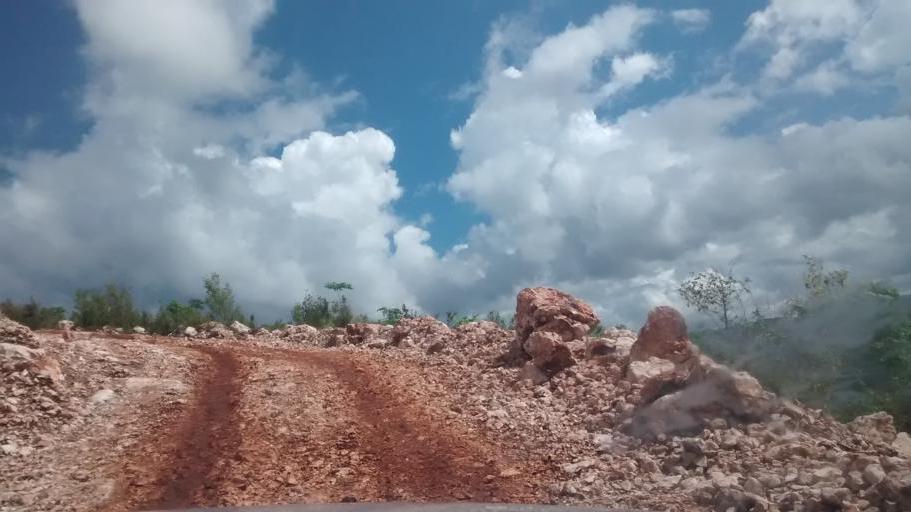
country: HT
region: Grandans
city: Corail
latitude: 18.5390
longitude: -73.9256
